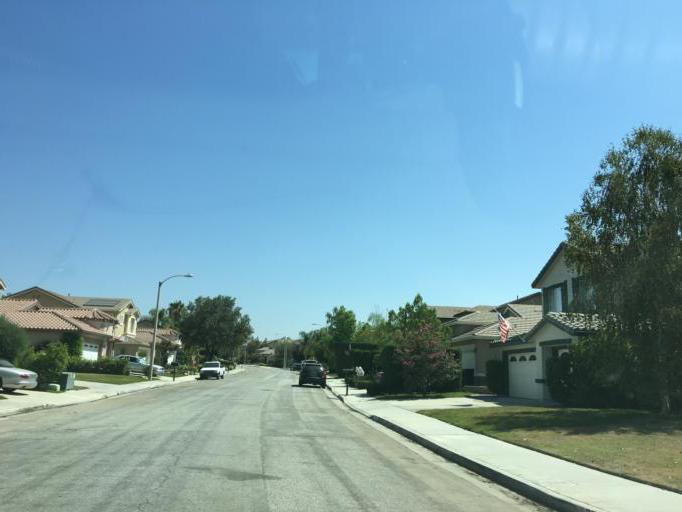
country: US
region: California
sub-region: Los Angeles County
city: Santa Clarita
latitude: 34.3940
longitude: -118.5912
